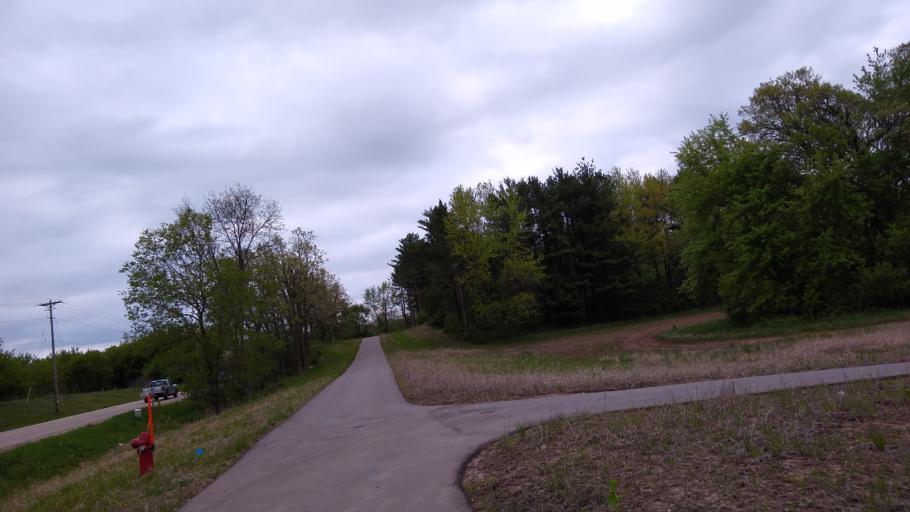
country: US
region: Wisconsin
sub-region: Dane County
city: Monona
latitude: 43.0137
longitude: -89.3754
